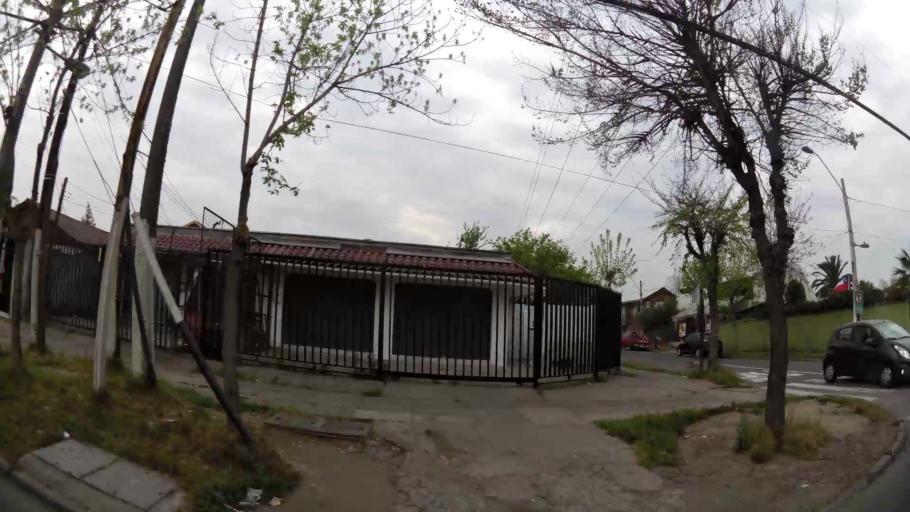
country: CL
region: Santiago Metropolitan
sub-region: Provincia de Santiago
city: Villa Presidente Frei, Nunoa, Santiago, Chile
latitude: -33.4974
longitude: -70.6020
